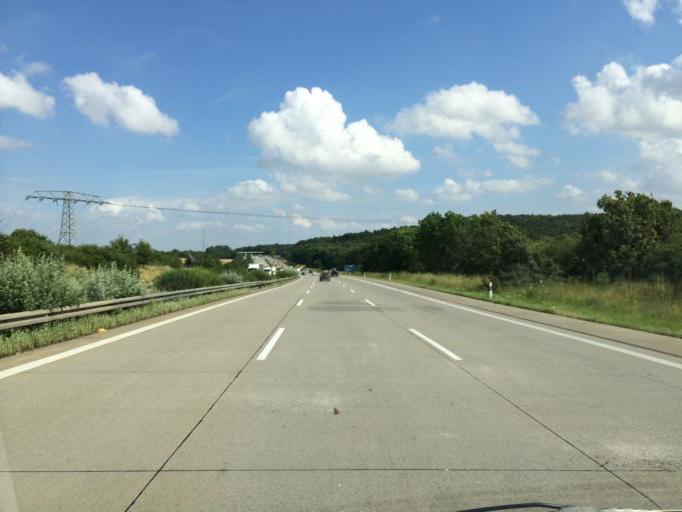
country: DE
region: Saxony-Anhalt
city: Beendorf
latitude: 52.2138
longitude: 11.0949
